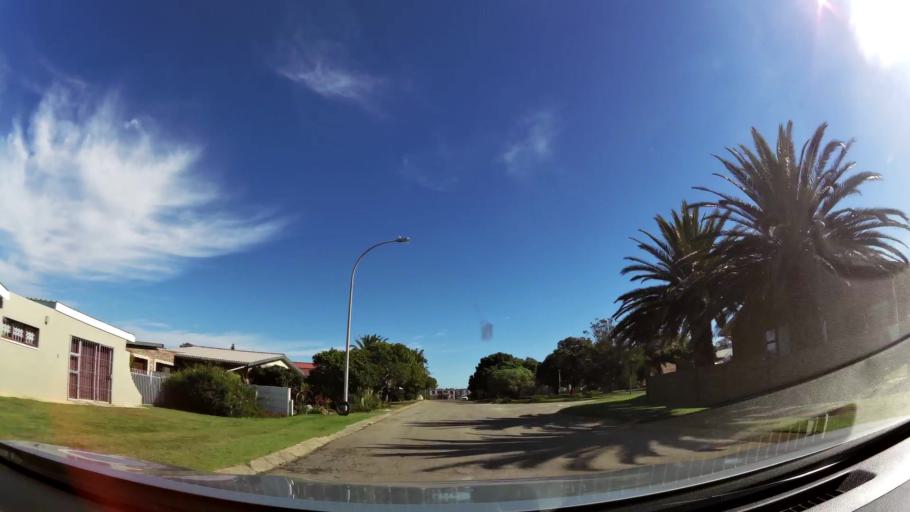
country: ZA
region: Eastern Cape
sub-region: Cacadu District Municipality
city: Jeffrey's Bay
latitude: -34.0505
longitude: 24.9155
